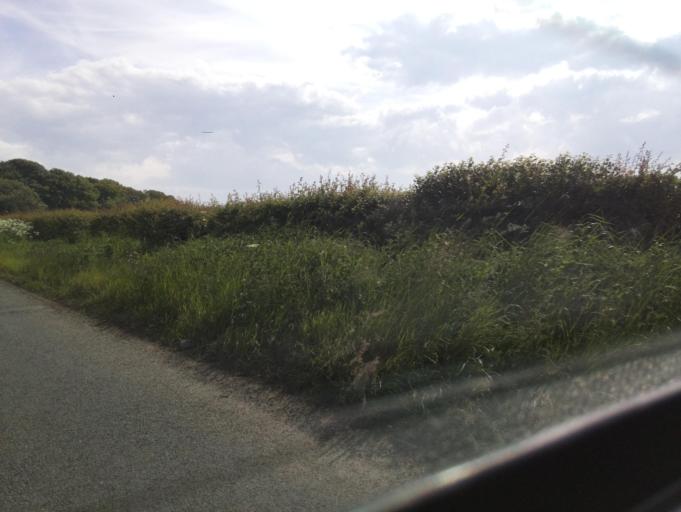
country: GB
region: England
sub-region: Northumberland
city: Alnwick
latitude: 55.4324
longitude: -1.7068
